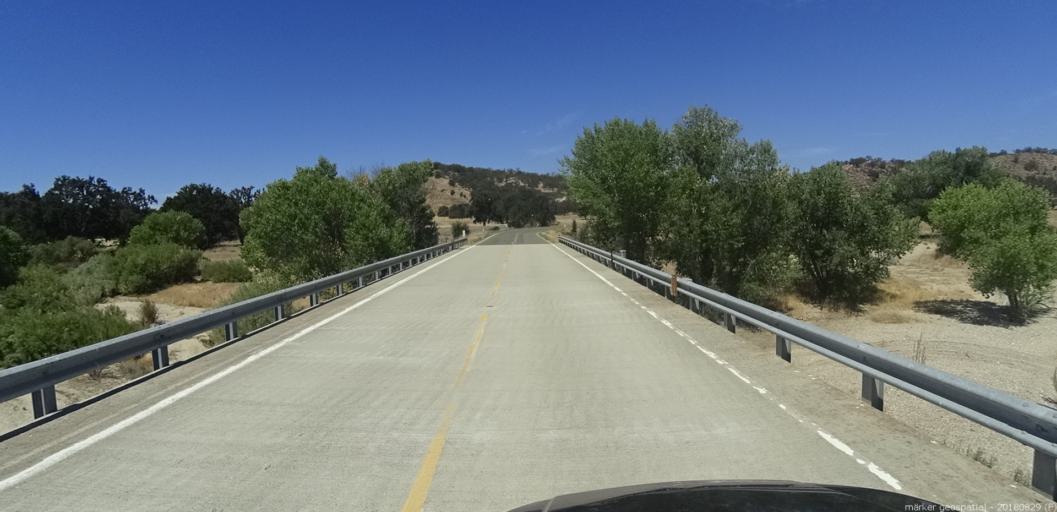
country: US
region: California
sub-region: San Luis Obispo County
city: Lake Nacimiento
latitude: 35.8967
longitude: -121.0884
